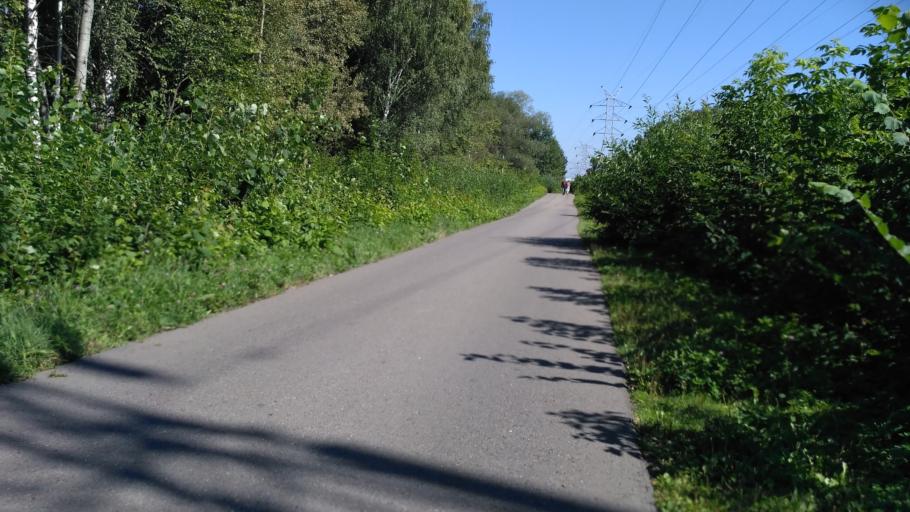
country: RU
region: Moscow
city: Metrogorodok
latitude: 55.7804
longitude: 37.7566
